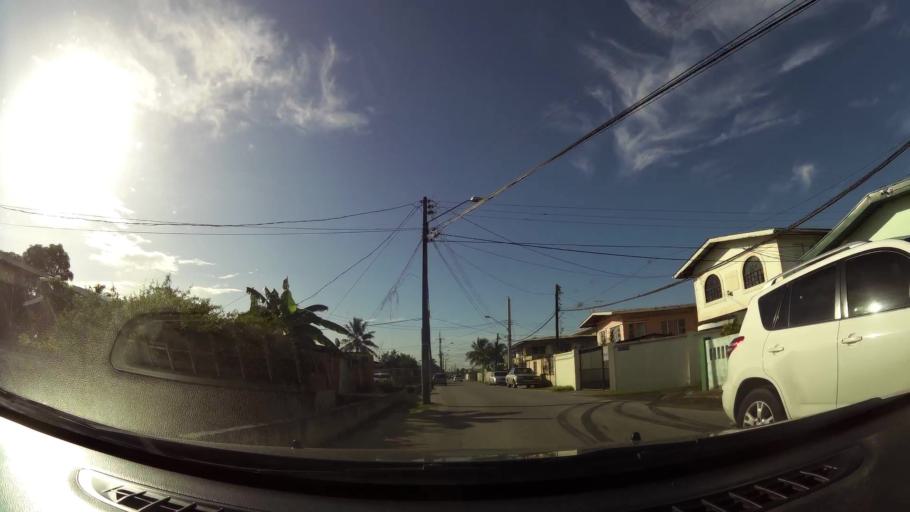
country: TT
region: Tunapuna/Piarco
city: Tunapuna
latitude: 10.5759
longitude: -61.3808
